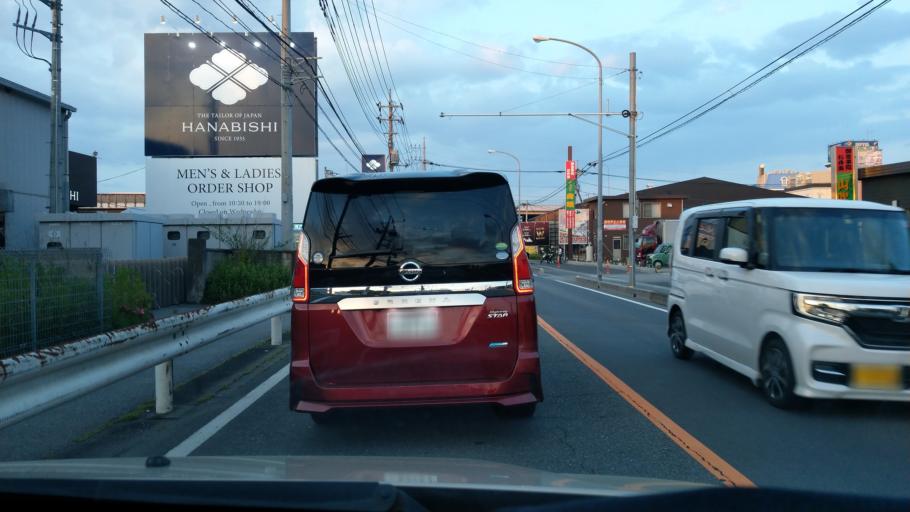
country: JP
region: Saitama
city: Iwatsuki
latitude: 35.9421
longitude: 139.6843
